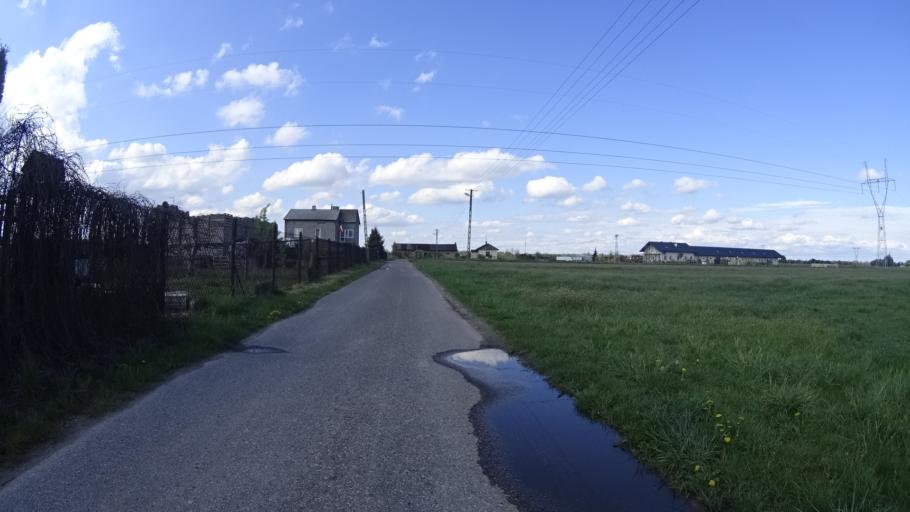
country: PL
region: Masovian Voivodeship
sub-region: Powiat warszawski zachodni
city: Jozefow
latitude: 52.2356
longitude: 20.6767
